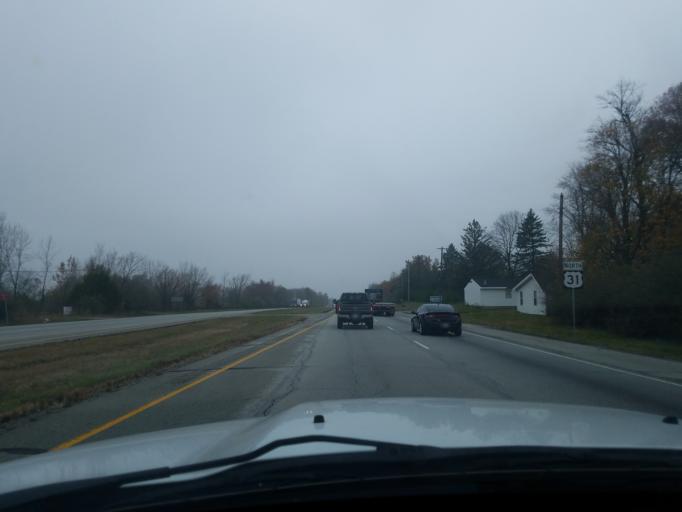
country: US
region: Indiana
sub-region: Hamilton County
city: Westfield
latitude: 40.1320
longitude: -86.1280
